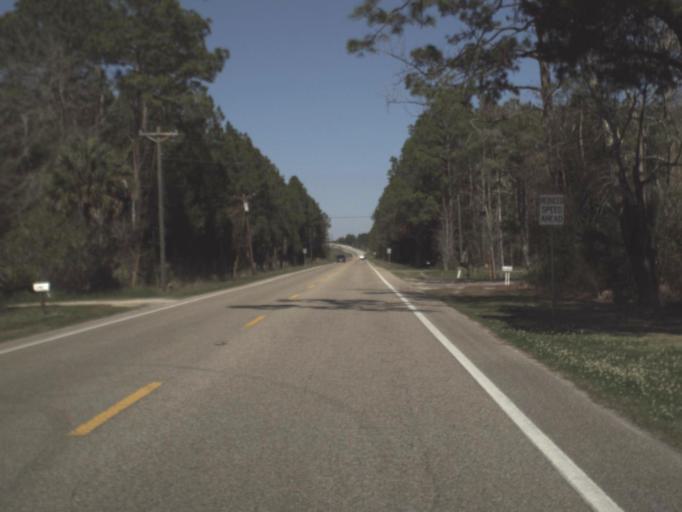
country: US
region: Florida
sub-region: Gulf County
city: Port Saint Joe
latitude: 29.8723
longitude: -85.2306
